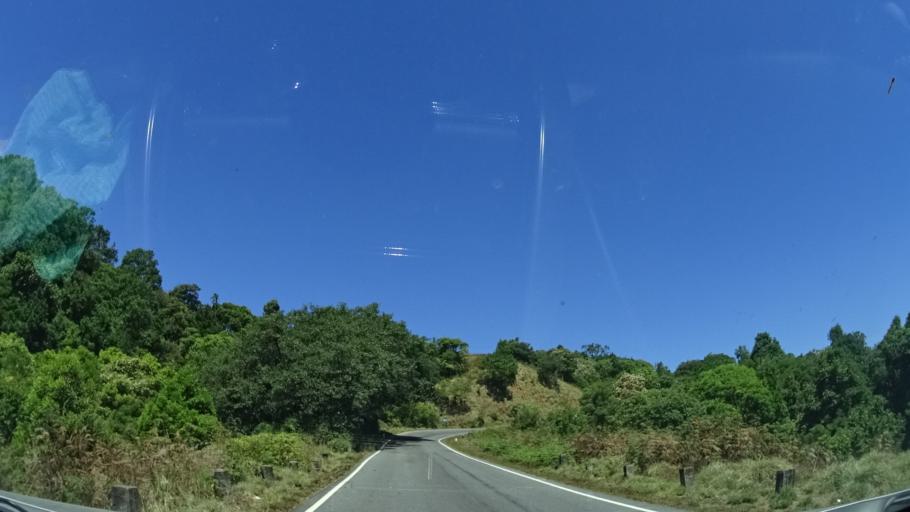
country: IN
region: Karnataka
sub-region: Udupi
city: Karkal
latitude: 13.2511
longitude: 75.1660
